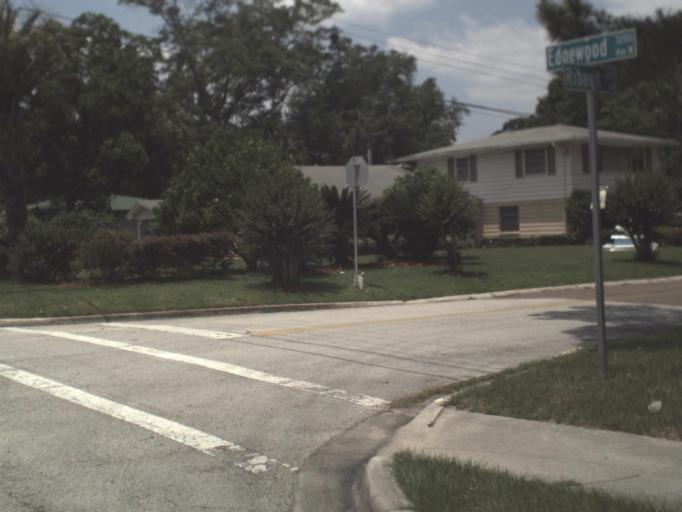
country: US
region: Florida
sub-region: Duval County
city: Jacksonville
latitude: 30.3716
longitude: -81.7222
